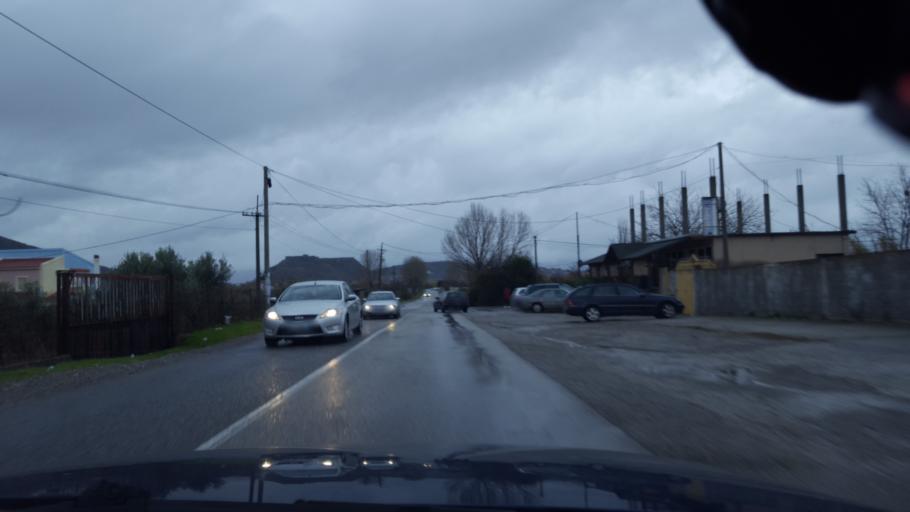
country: AL
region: Shkoder
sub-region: Rrethi i Shkodres
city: Berdica e Madhe
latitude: 42.0225
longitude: 19.4862
